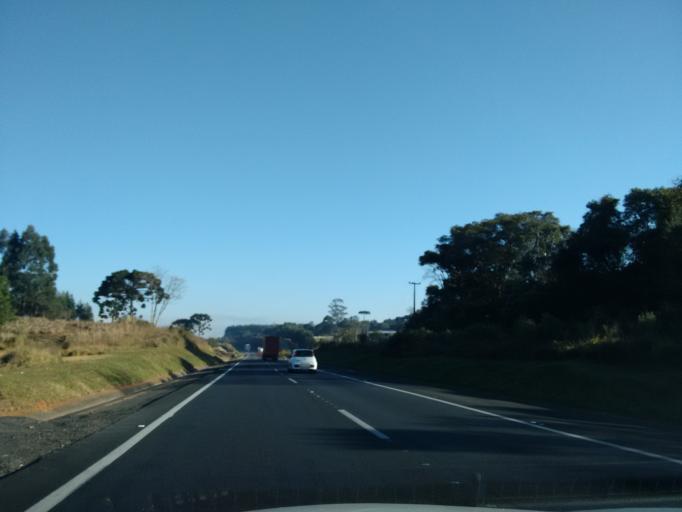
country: BR
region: Parana
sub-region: Campo Largo
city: Campo Largo
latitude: -25.4506
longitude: -49.5939
